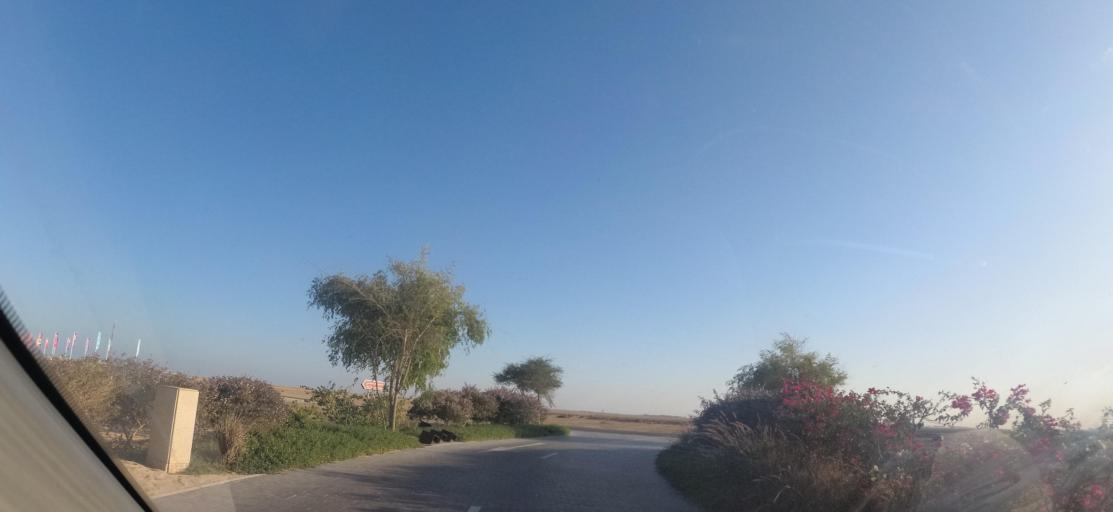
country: QA
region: Madinat ash Shamal
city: Ar Ru'ays
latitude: 26.1554
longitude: 51.2447
